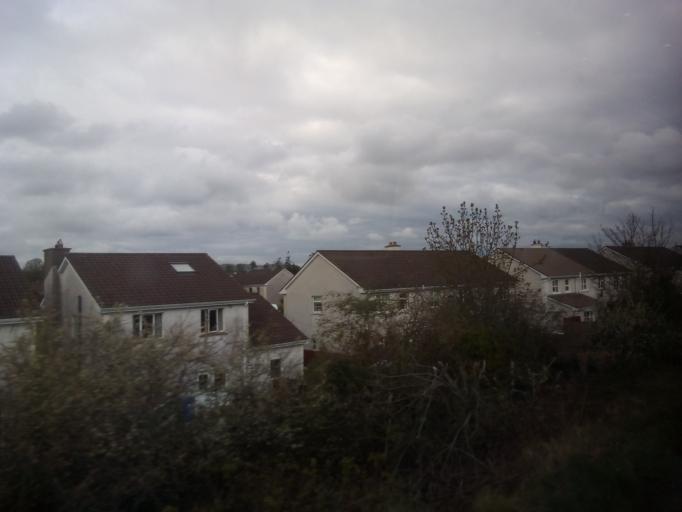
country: IE
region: Leinster
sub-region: An Longfort
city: Longford
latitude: 53.7264
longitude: -7.7831
